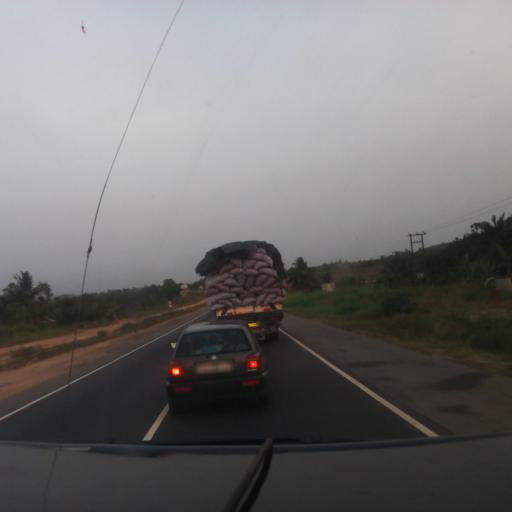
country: GH
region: Eastern
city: Nsawam
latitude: 5.8929
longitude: -0.3835
